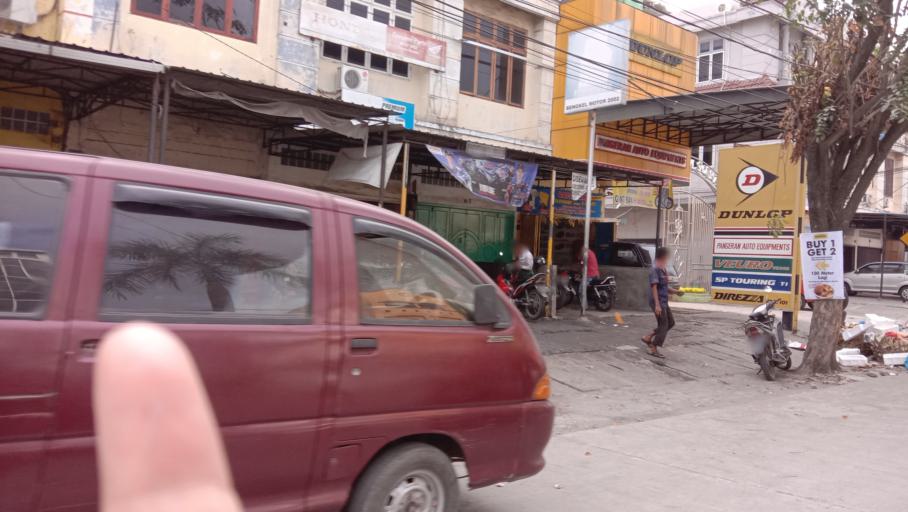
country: ID
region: North Sumatra
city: Medan
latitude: 3.6028
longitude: 98.6454
